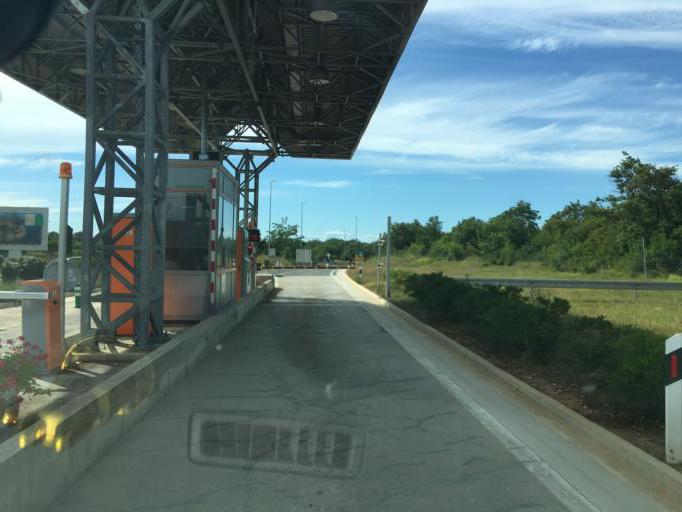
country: HR
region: Istarska
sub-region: Grad Rovinj
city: Rovinj
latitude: 45.1511
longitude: 13.7422
